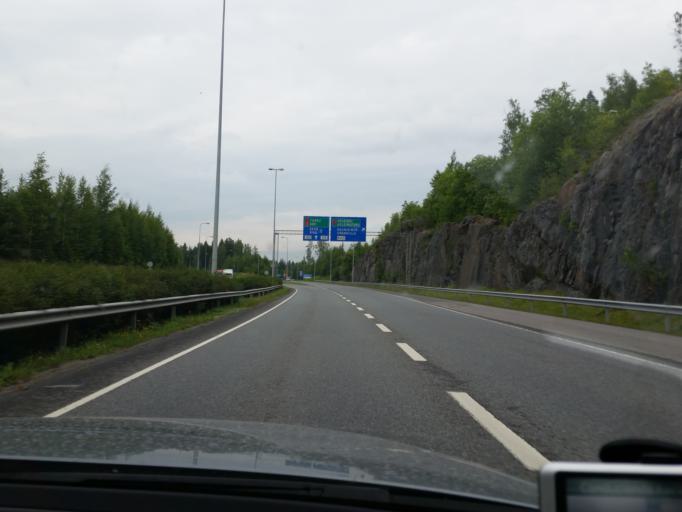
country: FI
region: Uusimaa
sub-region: Helsinki
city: Kauniainen
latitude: 60.1984
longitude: 24.7453
